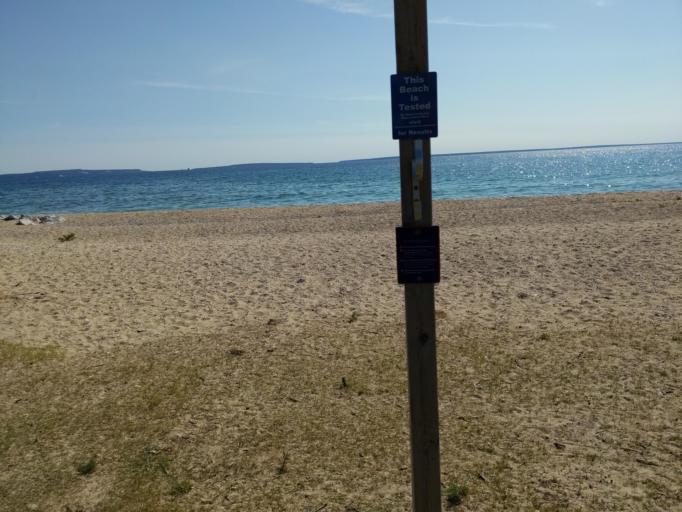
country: US
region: Michigan
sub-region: Mackinac County
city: Saint Ignace
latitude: 45.7833
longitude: -84.7232
